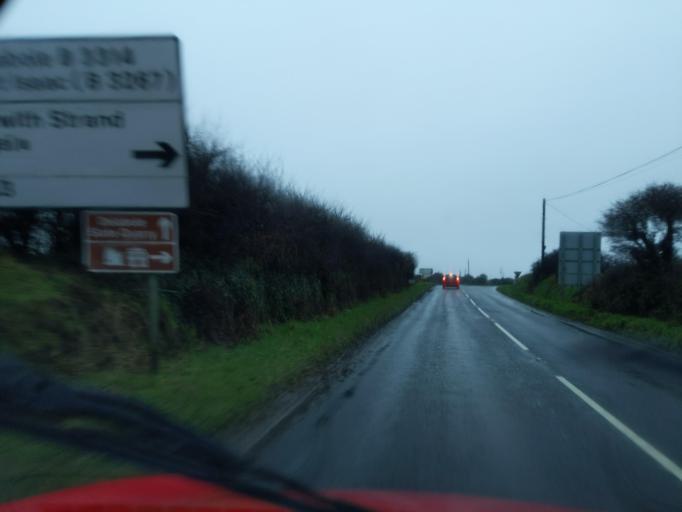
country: GB
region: England
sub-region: Cornwall
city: Camelford
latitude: 50.6388
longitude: -4.6912
